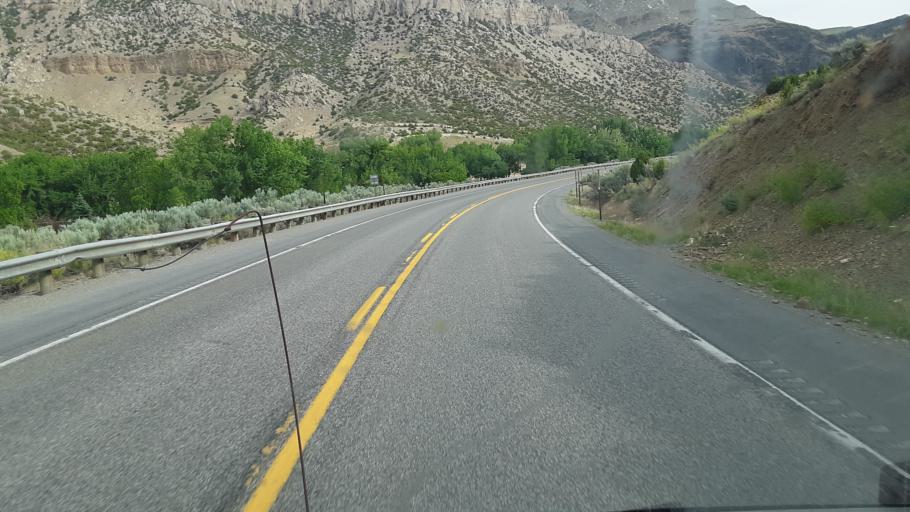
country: US
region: Wyoming
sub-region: Hot Springs County
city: Thermopolis
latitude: 43.4304
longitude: -108.1780
